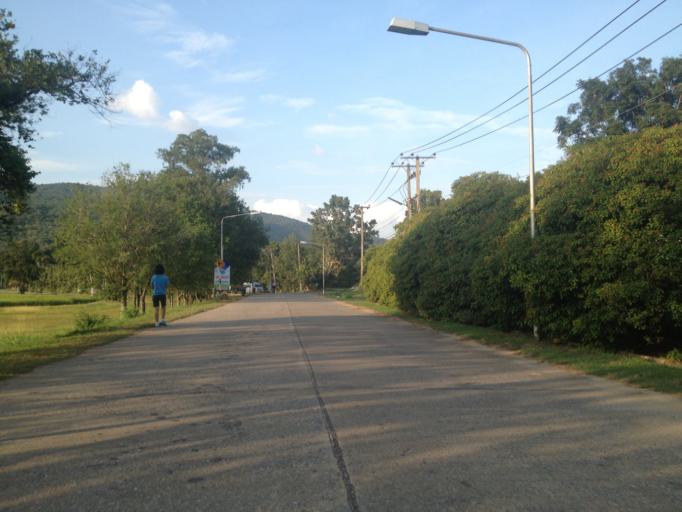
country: TH
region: Chiang Mai
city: Chiang Mai
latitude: 18.7606
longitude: 98.9322
